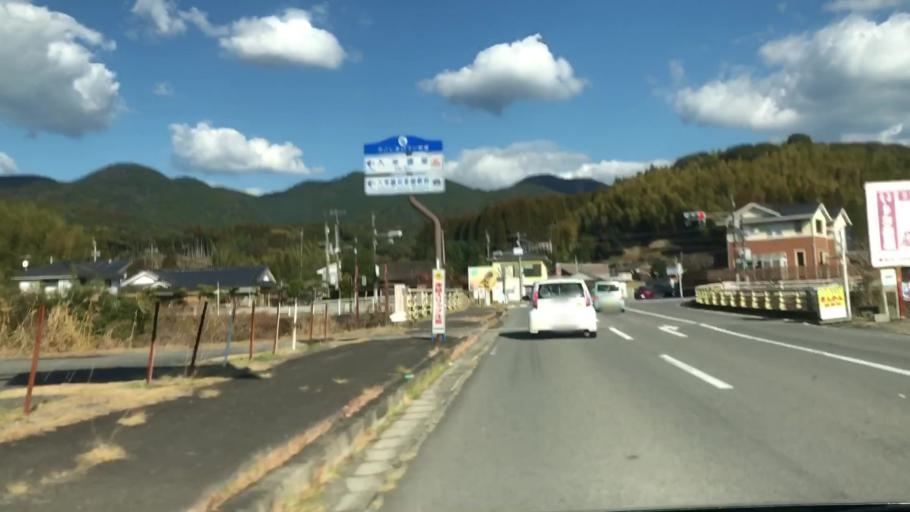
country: JP
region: Kagoshima
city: Satsumasendai
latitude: 31.7953
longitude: 130.4415
